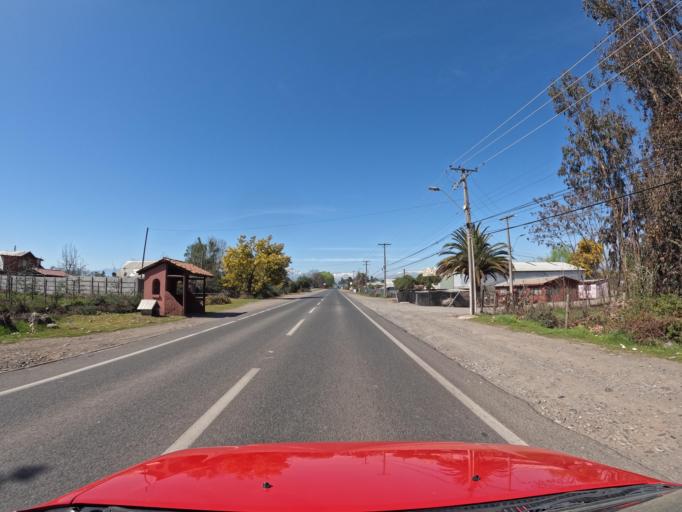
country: CL
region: Maule
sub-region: Provincia de Curico
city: Teno
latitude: -34.9620
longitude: -71.0864
